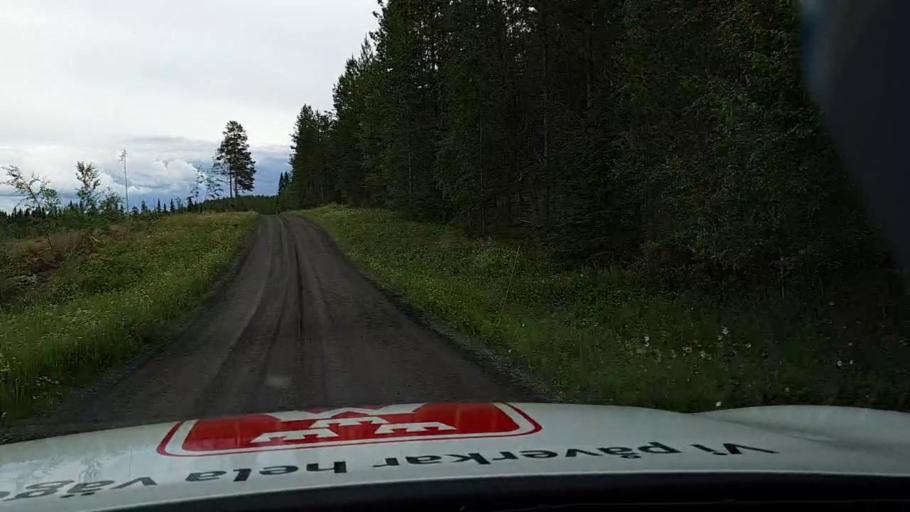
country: SE
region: Jaemtland
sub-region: OEstersunds Kommun
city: Lit
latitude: 63.5626
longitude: 14.7269
